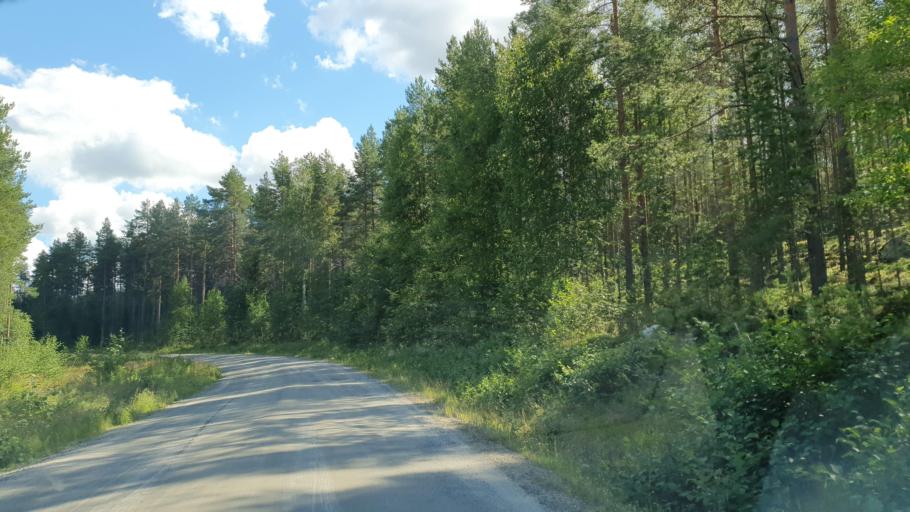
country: FI
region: Kainuu
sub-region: Kehys-Kainuu
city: Kuhmo
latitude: 64.0993
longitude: 29.4047
